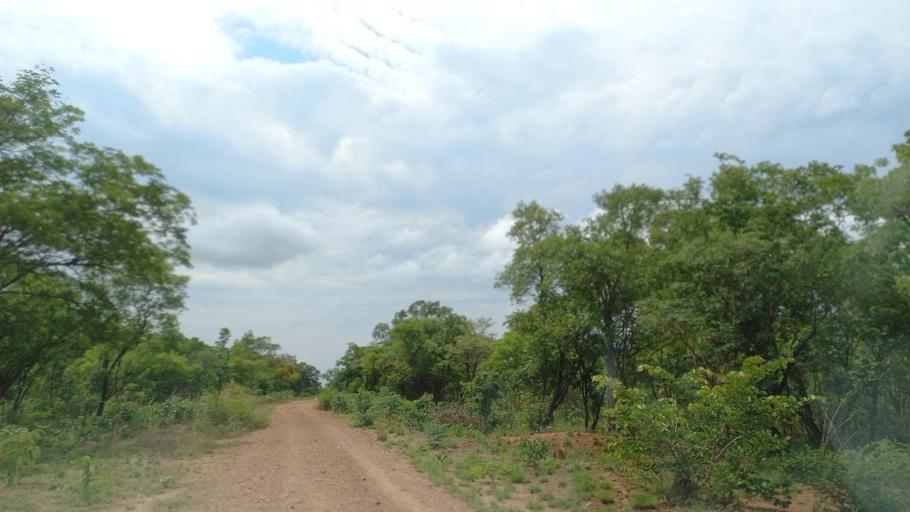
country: ZM
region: North-Western
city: Kalengwa
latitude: -13.4594
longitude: 25.0055
